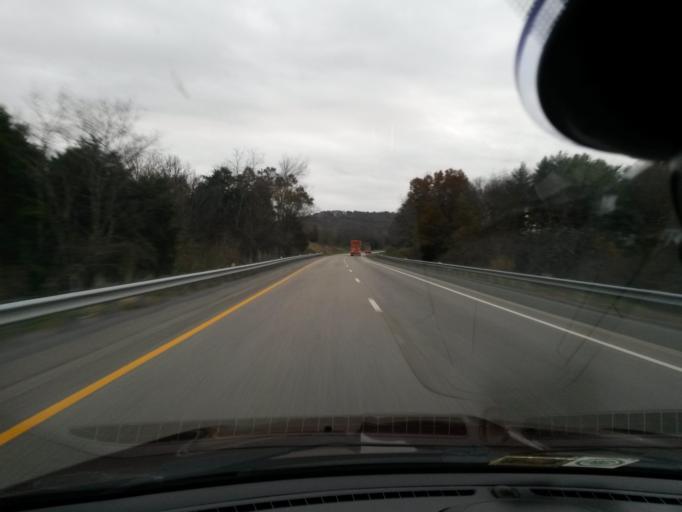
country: US
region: Virginia
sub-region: Rockbridge County
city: East Lexington
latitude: 37.8456
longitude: -79.4609
